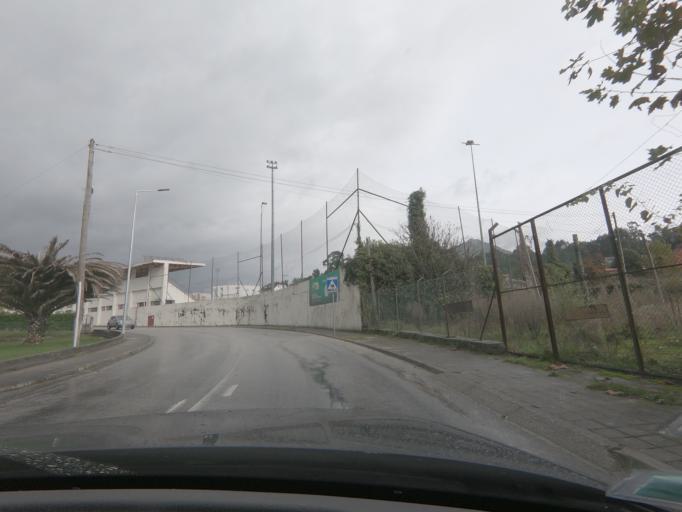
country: PT
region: Vila Real
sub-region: Mondim de Basto
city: Mondim de Basto
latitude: 41.4063
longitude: -7.9562
